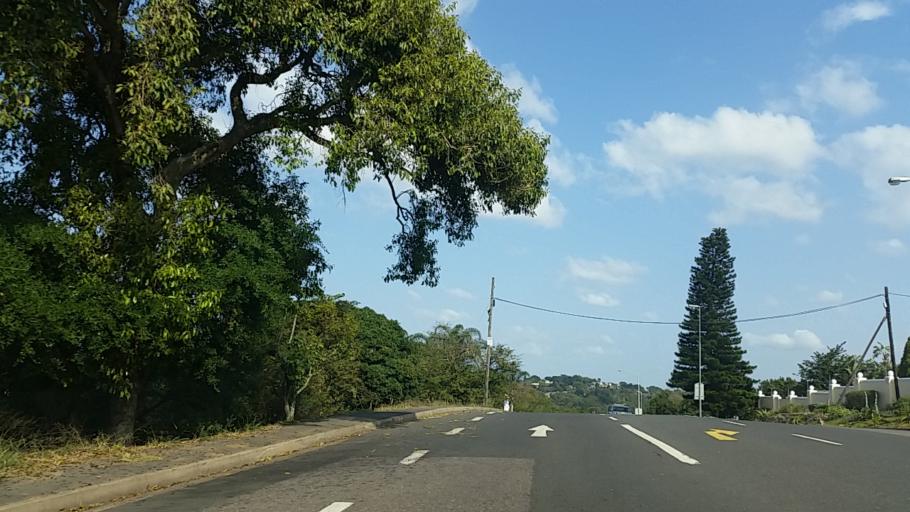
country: ZA
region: KwaZulu-Natal
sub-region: eThekwini Metropolitan Municipality
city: Berea
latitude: -29.8329
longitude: 30.9211
